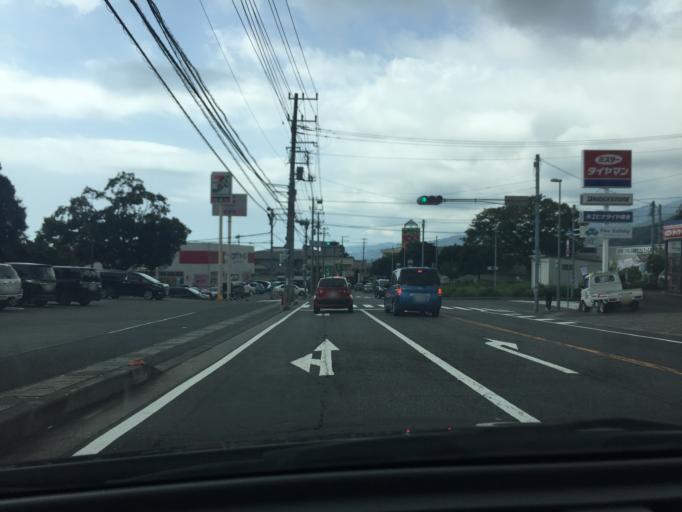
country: JP
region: Shizuoka
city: Ito
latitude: 34.8778
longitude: 139.1047
